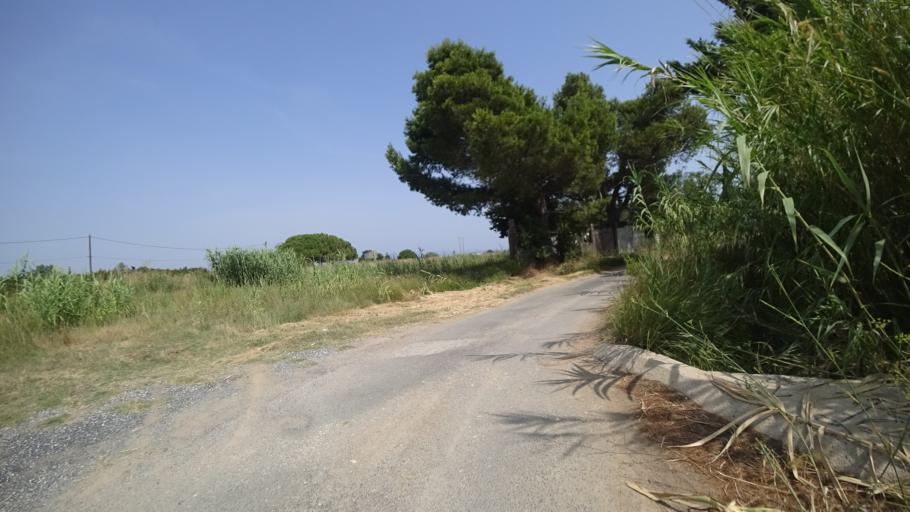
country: FR
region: Languedoc-Roussillon
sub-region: Departement des Pyrenees-Orientales
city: Le Barcares
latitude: 42.7806
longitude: 3.0156
